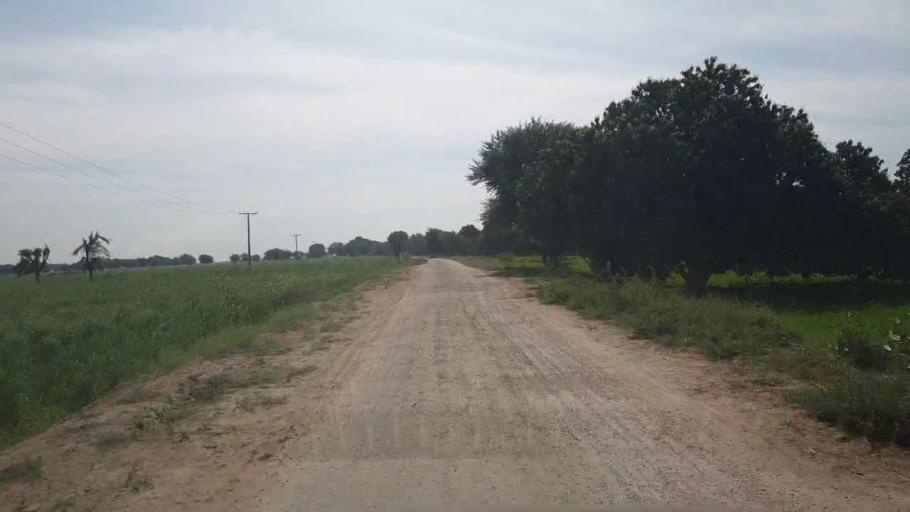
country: PK
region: Sindh
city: Umarkot
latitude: 25.3423
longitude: 69.5925
